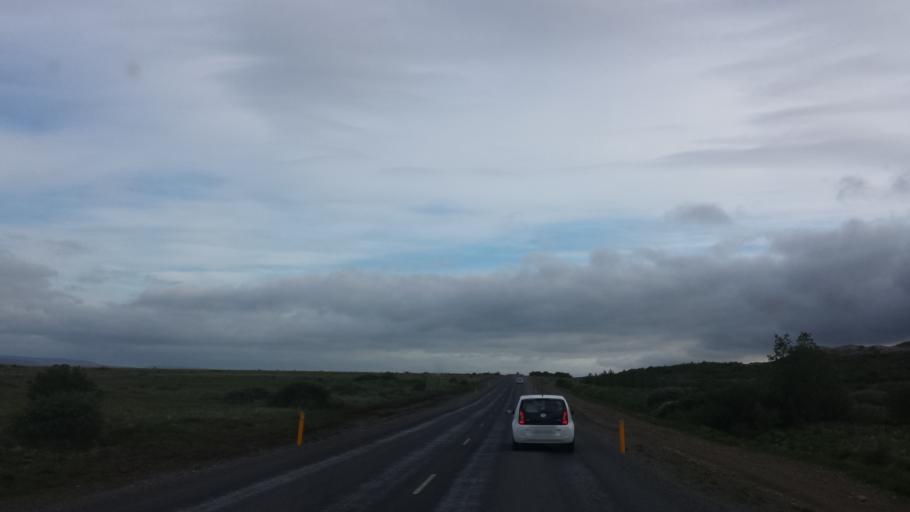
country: IS
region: South
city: Selfoss
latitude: 64.2923
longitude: -20.3363
